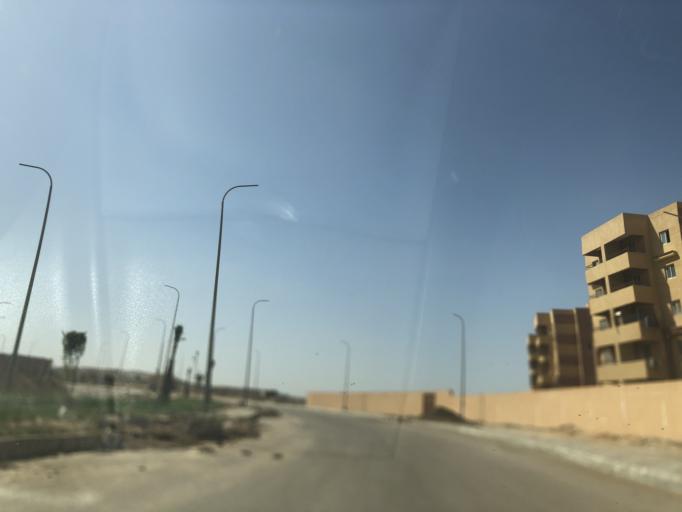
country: EG
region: Al Jizah
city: Madinat Sittah Uktubar
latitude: 29.9264
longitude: 31.0427
